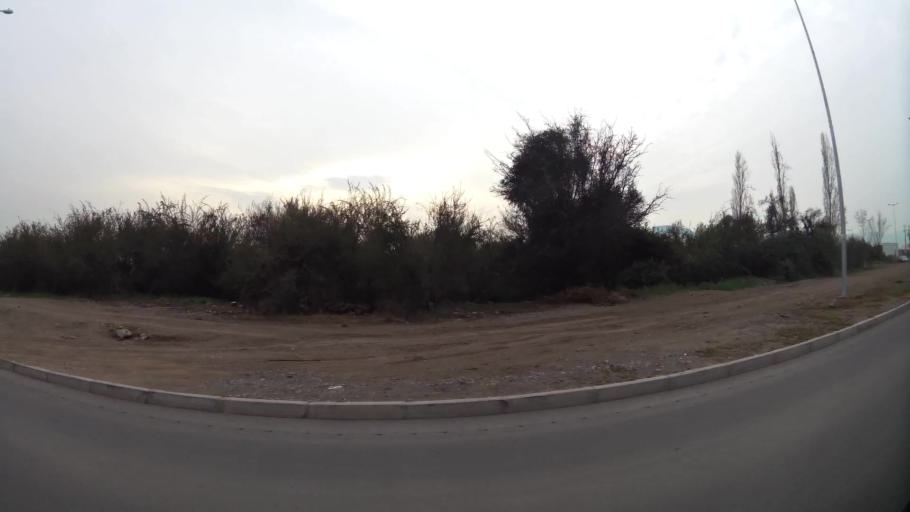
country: CL
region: Santiago Metropolitan
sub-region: Provincia de Chacabuco
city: Chicureo Abajo
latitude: -33.2621
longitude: -70.6186
